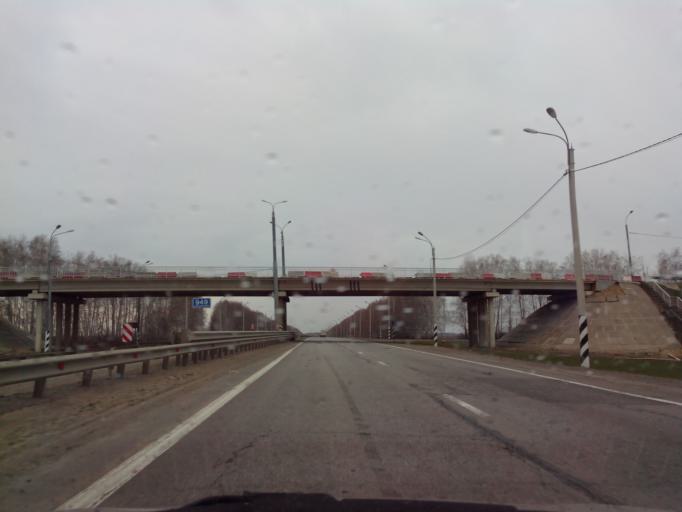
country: RU
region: Tambov
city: Selezni
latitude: 52.7600
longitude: 41.1360
